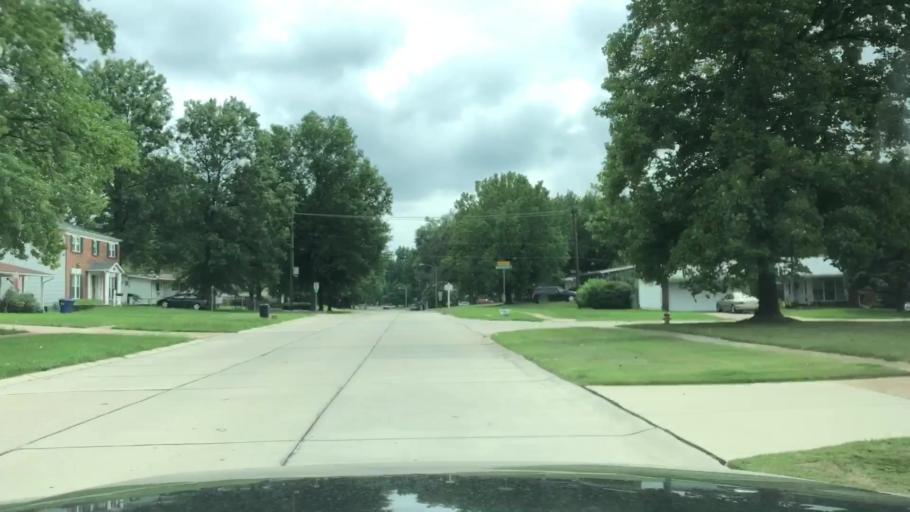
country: US
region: Missouri
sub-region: Saint Louis County
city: Florissant
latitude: 38.8071
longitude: -90.3153
